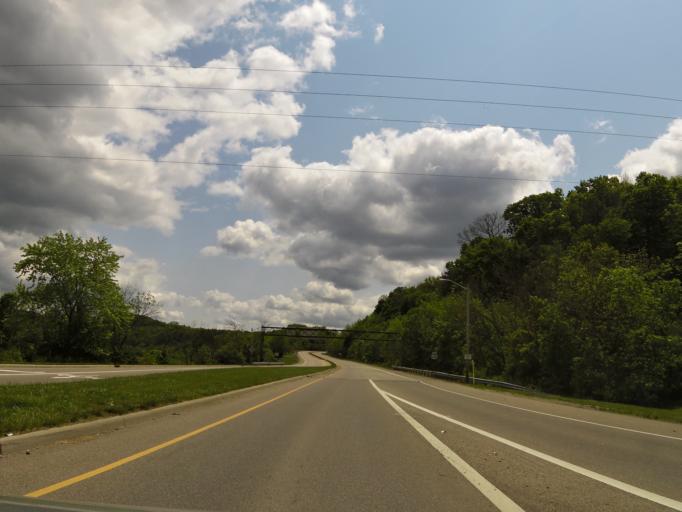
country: US
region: Ohio
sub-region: Athens County
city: Athens
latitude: 39.3189
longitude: -82.1053
